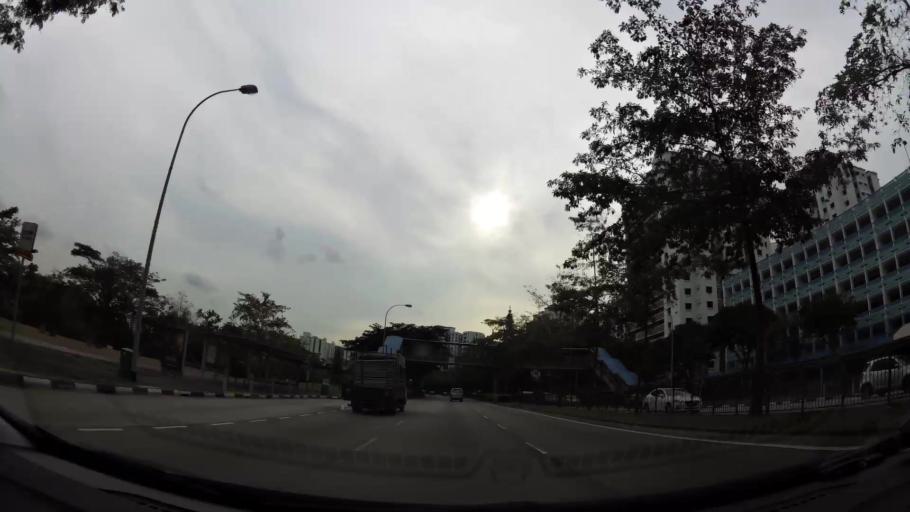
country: MY
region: Johor
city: Kampung Pasir Gudang Baru
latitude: 1.3859
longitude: 103.9064
